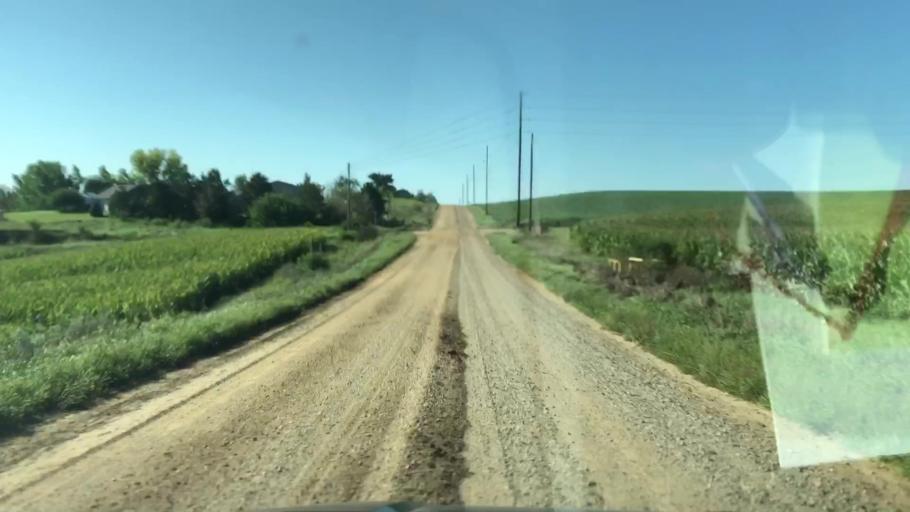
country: US
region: Iowa
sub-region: Woodbury County
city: Sergeant Bluff
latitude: 42.4630
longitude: -96.2526
